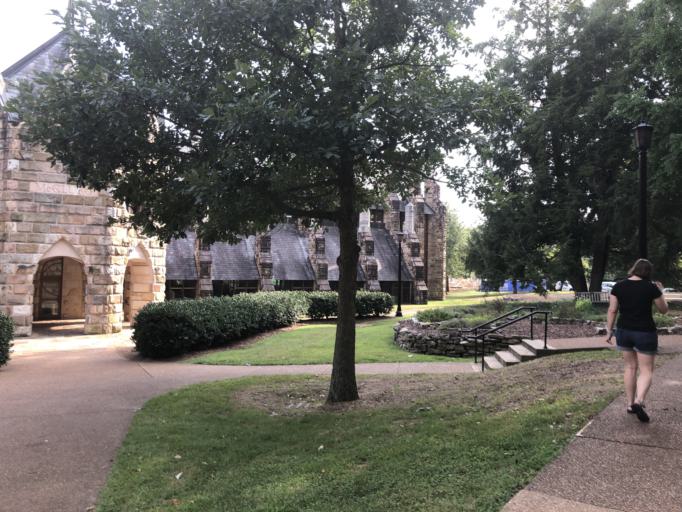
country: US
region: Tennessee
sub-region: Franklin County
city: Sewanee
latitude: 35.2036
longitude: -85.9202
